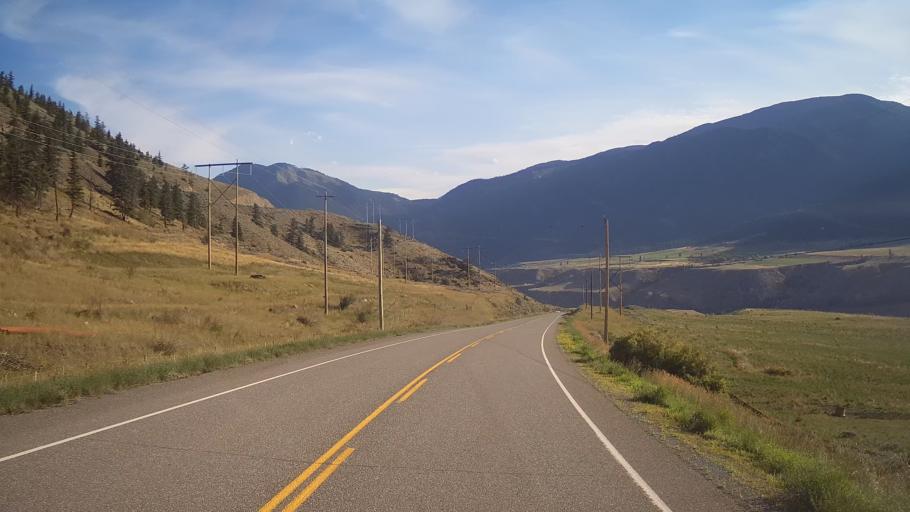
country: CA
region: British Columbia
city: Lillooet
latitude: 50.8615
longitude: -121.8551
